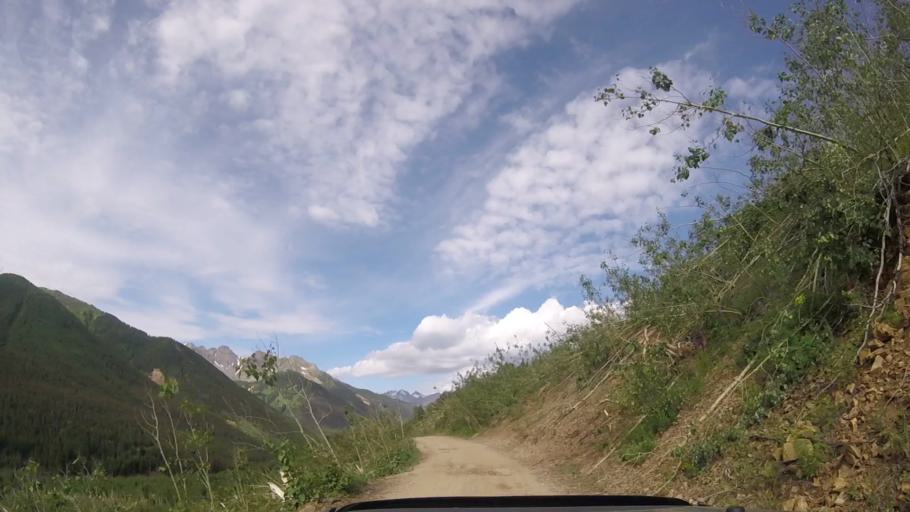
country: US
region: Colorado
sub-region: San Miguel County
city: Telluride
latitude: 37.8594
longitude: -107.8021
